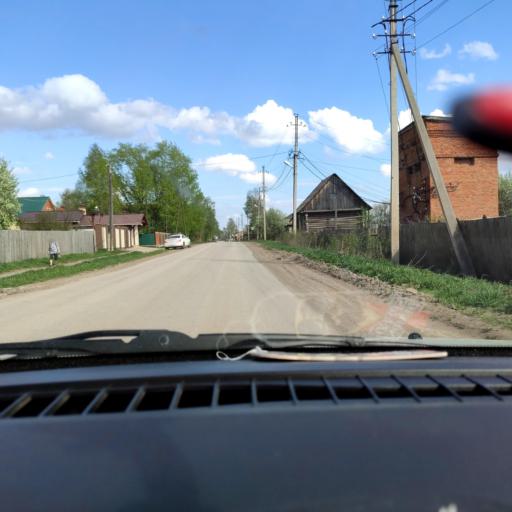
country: RU
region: Perm
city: Kudymkar
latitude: 59.0074
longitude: 54.6585
